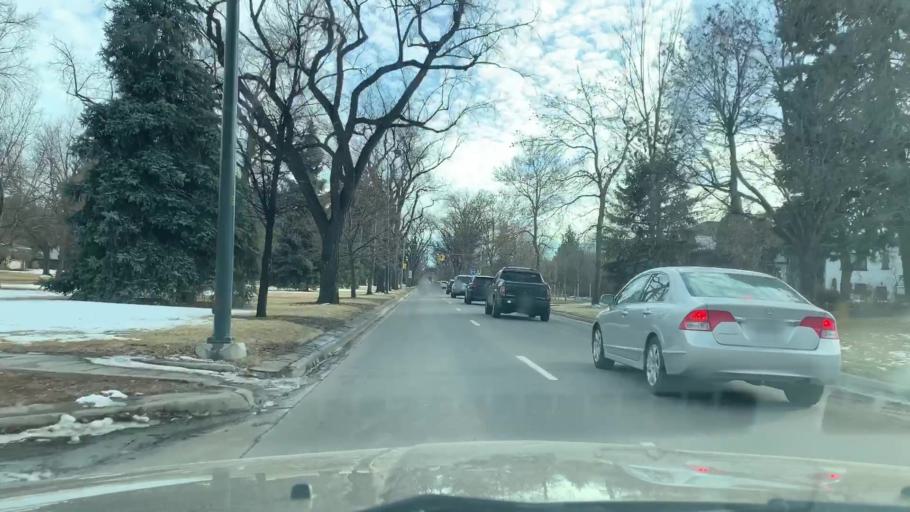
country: US
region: Colorado
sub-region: Arapahoe County
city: Glendale
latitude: 39.7304
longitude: -104.9128
